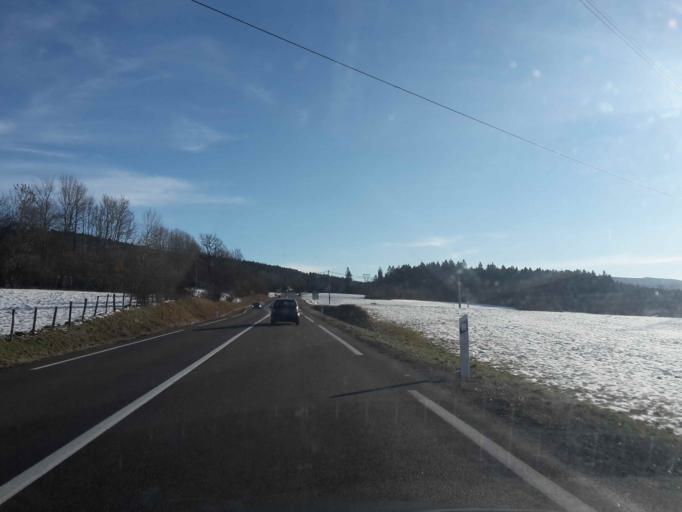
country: FR
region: Franche-Comte
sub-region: Departement du Doubs
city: Doubs
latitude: 47.0178
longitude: 6.3252
